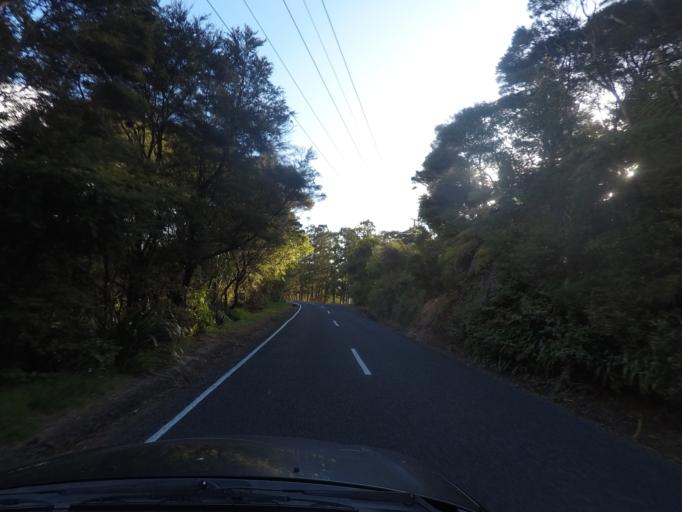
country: NZ
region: Auckland
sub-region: Auckland
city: Titirangi
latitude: -36.9284
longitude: 174.6199
